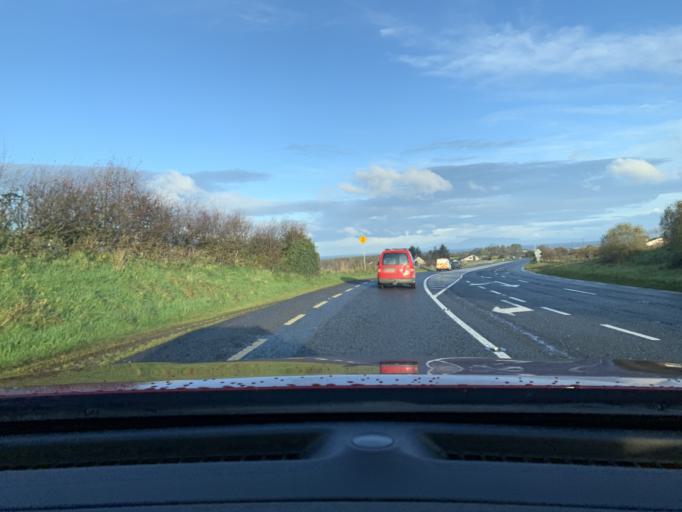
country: IE
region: Connaught
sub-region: Sligo
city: Strandhill
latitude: 54.3667
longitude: -8.5301
